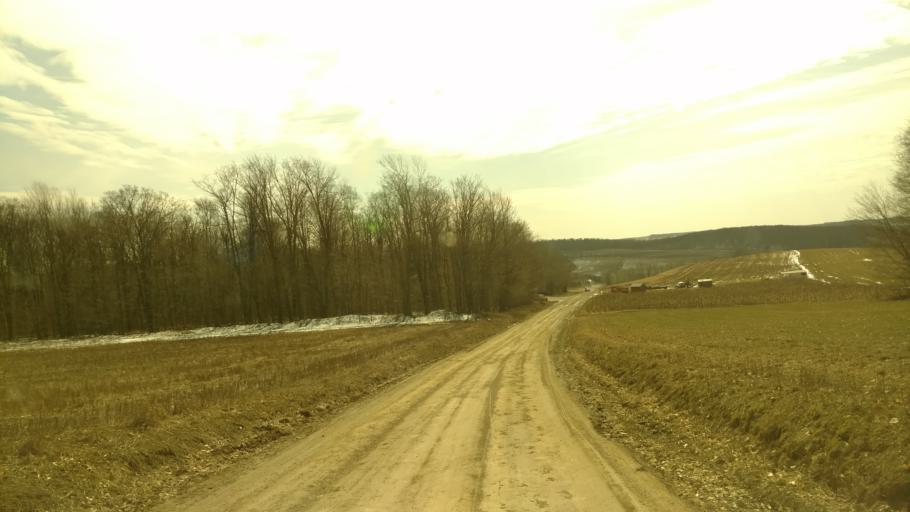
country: US
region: New York
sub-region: Allegany County
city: Andover
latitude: 41.9361
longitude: -77.7682
